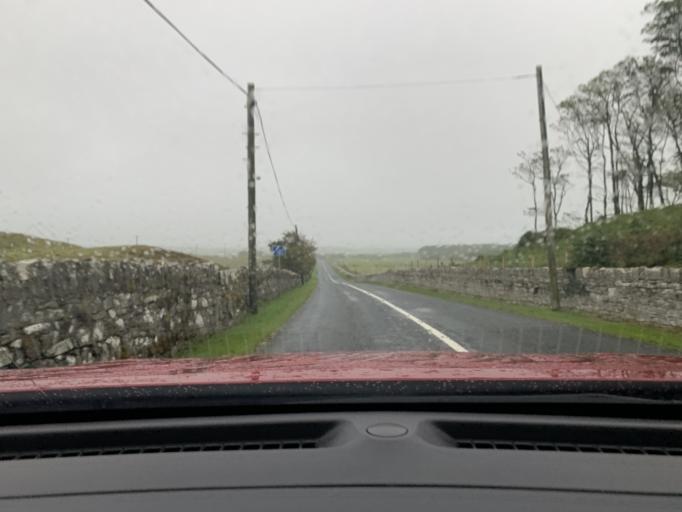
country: IE
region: Connaught
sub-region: County Leitrim
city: Kinlough
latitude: 54.4571
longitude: -8.4559
